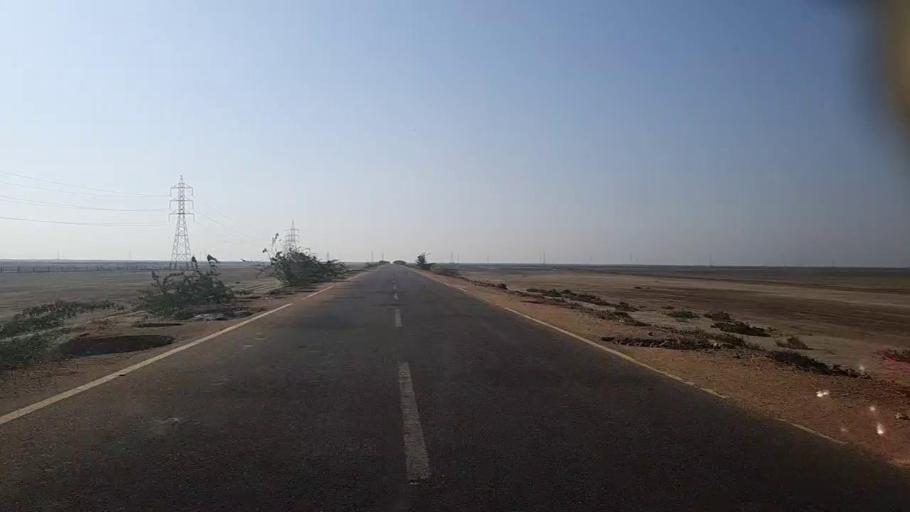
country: PK
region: Sindh
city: Mirpur Sakro
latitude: 24.6043
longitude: 67.4976
